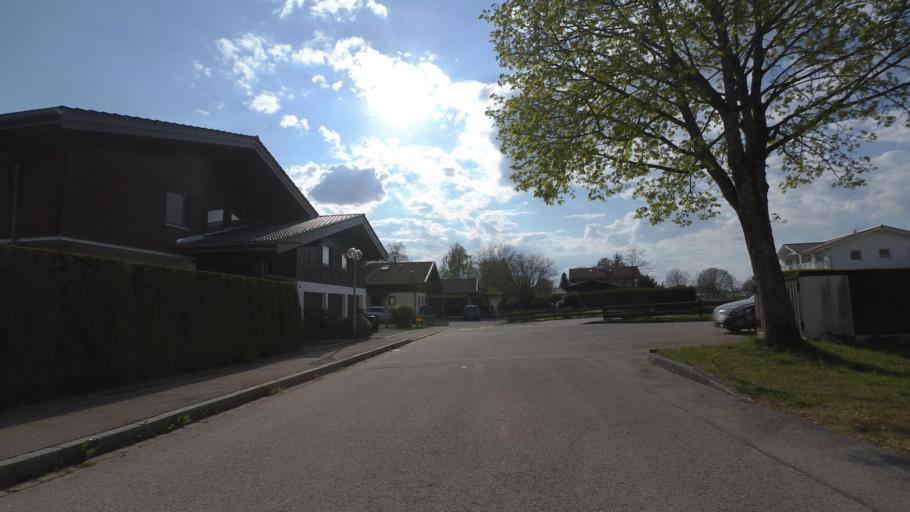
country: DE
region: Bavaria
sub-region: Upper Bavaria
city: Seeon-Seebruck
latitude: 47.9341
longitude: 12.4715
